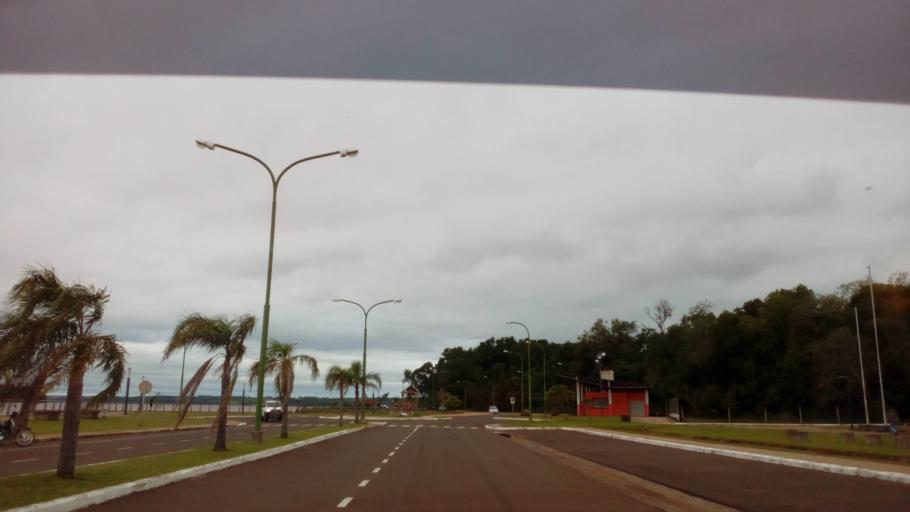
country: AR
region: Misiones
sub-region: Departamento de Candelaria
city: Candelaria
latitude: -27.4488
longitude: -55.7512
